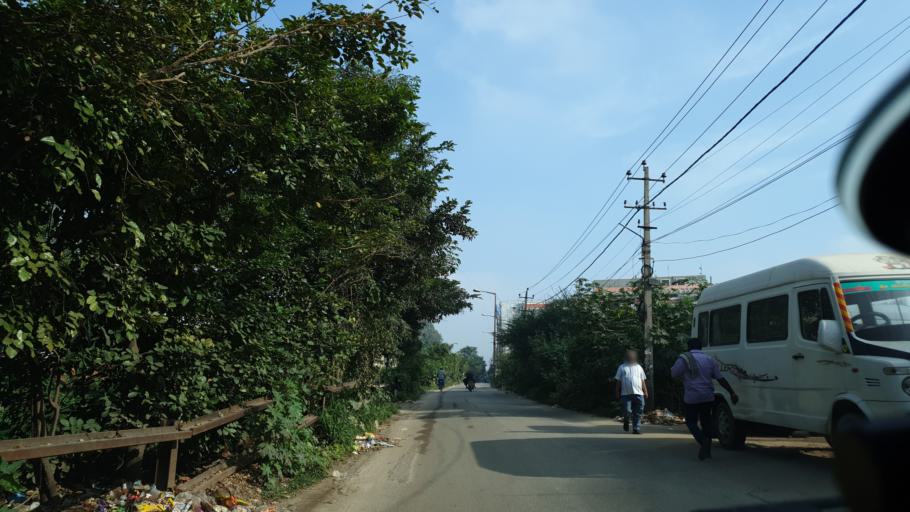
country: IN
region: Karnataka
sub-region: Bangalore Urban
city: Bangalore
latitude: 12.9593
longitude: 77.7044
